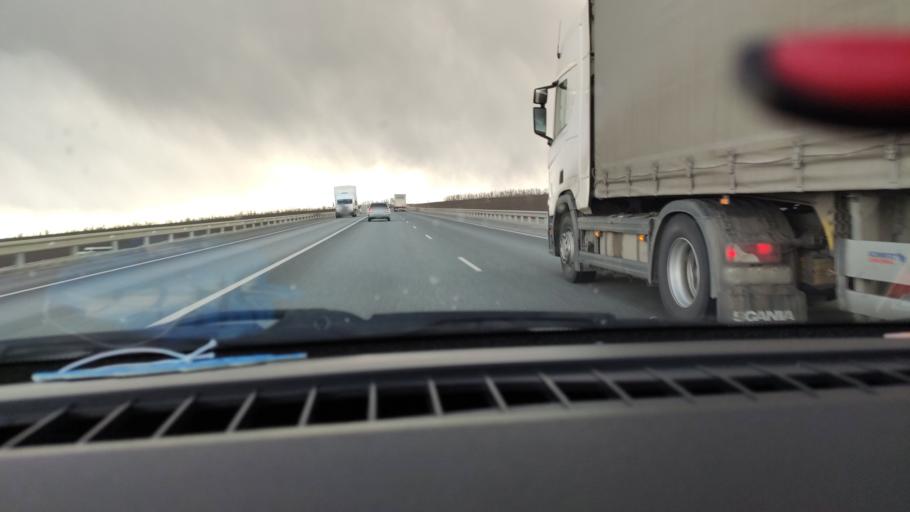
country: RU
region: Saratov
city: Yelshanka
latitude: 51.8381
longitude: 46.4746
